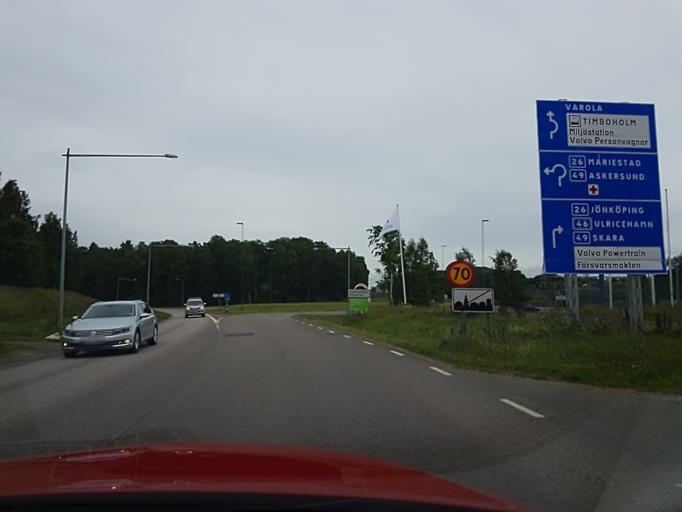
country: SE
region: Vaestra Goetaland
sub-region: Skovde Kommun
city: Skoevde
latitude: 58.3820
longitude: 13.8697
